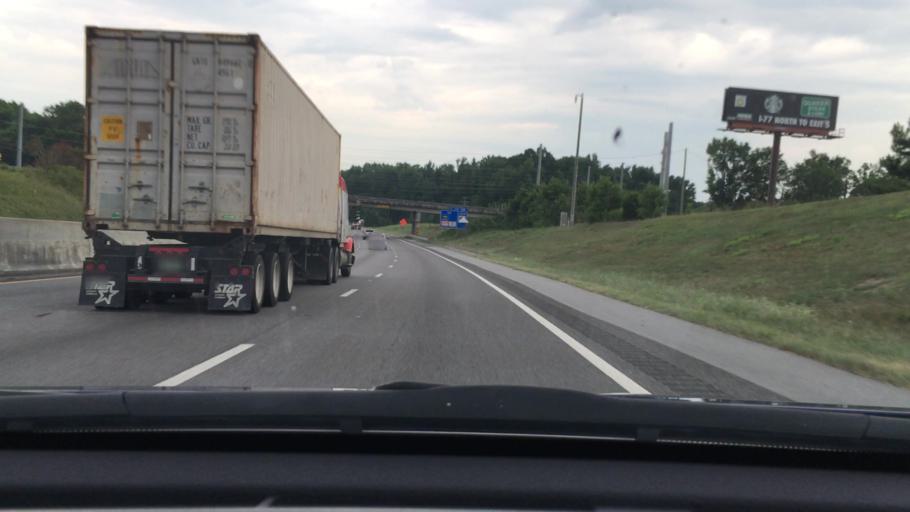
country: US
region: South Carolina
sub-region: Lexington County
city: Springdale
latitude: 33.9399
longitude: -81.0875
